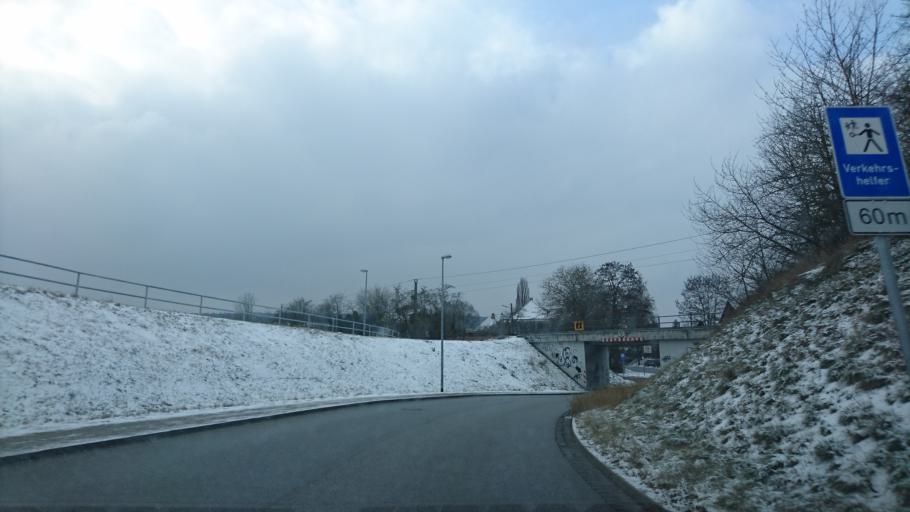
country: DE
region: Bavaria
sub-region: Upper Palatinate
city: Sinzing
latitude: 49.0106
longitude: 12.0399
